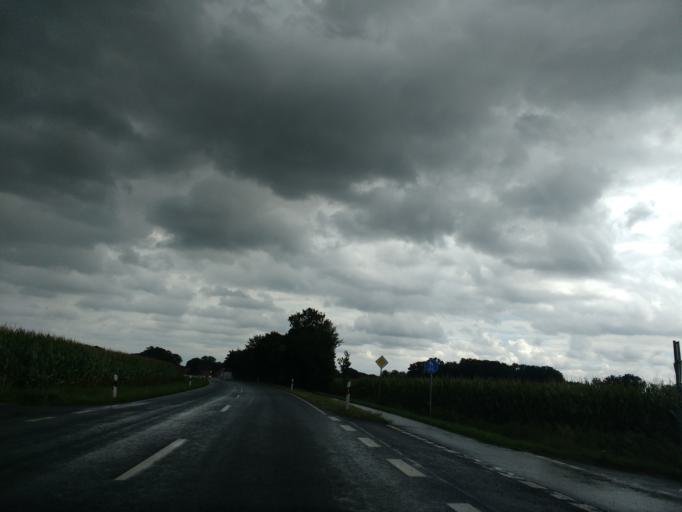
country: DE
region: Lower Saxony
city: Glandorf
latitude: 52.0894
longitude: 7.9735
